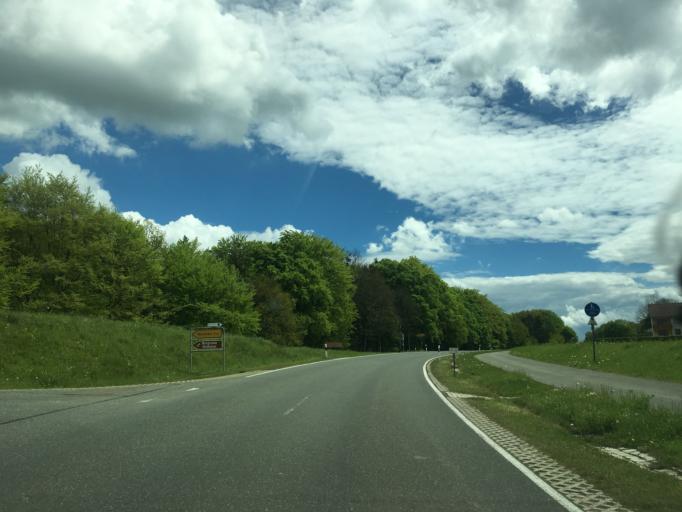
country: DE
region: Bavaria
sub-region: Upper Palatinate
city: Pilsach
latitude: 49.2873
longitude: 11.5028
